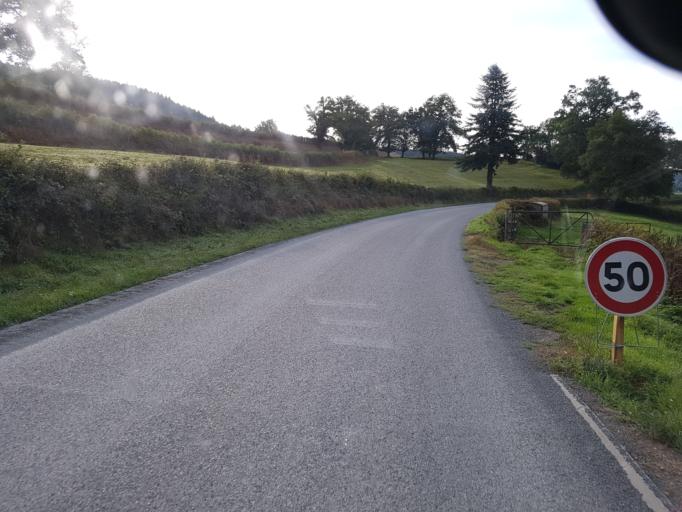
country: FR
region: Bourgogne
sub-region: Departement de Saone-et-Loire
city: Chauffailles
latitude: 46.2634
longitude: 4.4008
